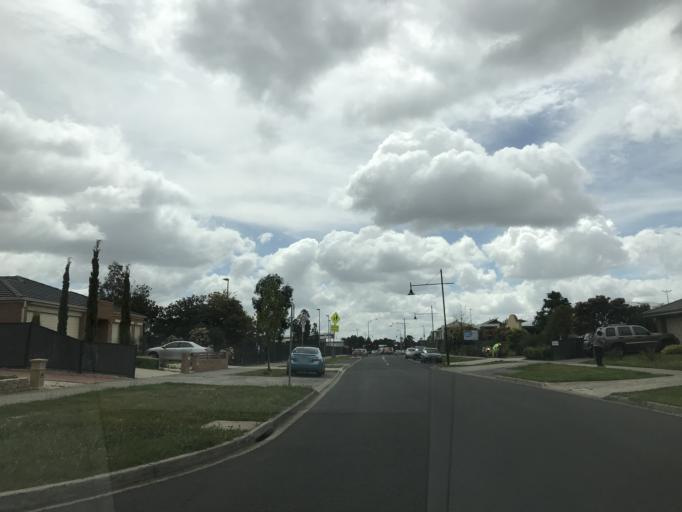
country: AU
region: Victoria
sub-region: Brimbank
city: Derrimut
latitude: -37.7932
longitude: 144.7608
